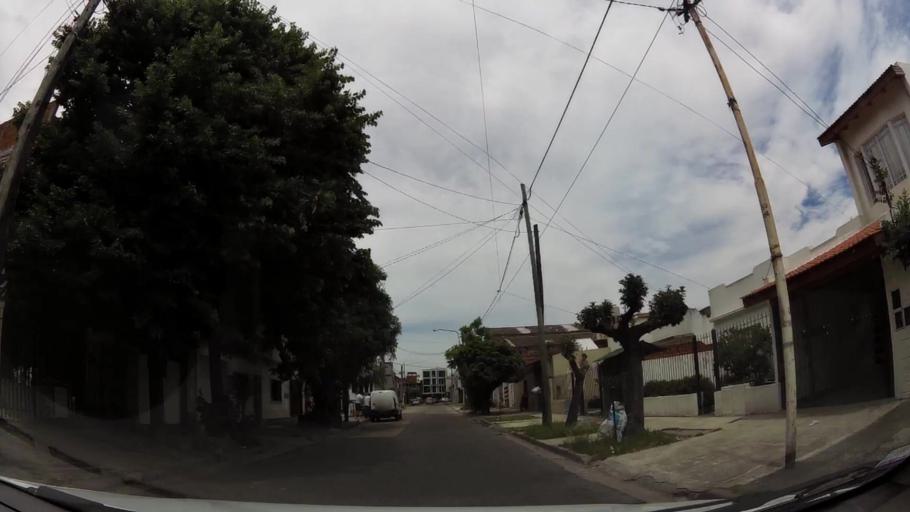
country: AR
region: Buenos Aires
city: San Justo
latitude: -34.6747
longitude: -58.5462
